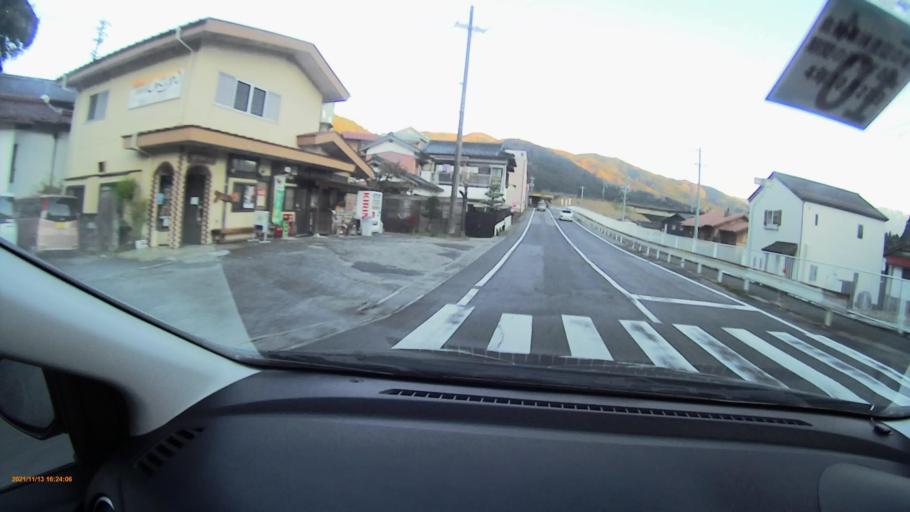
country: JP
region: Gifu
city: Nakatsugawa
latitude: 35.5724
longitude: 137.5291
